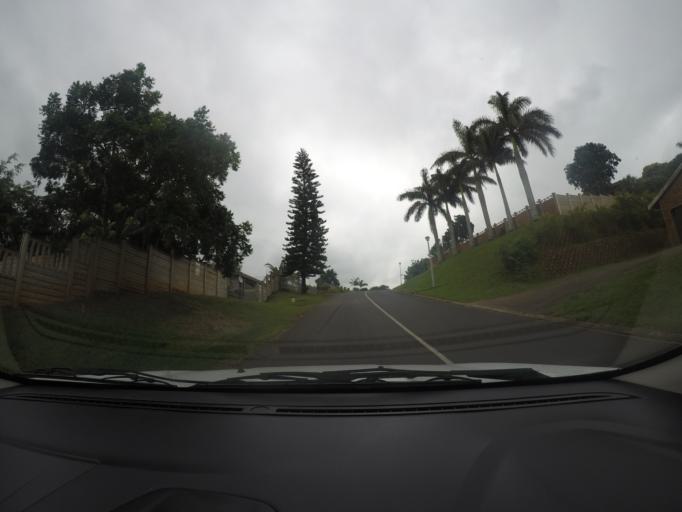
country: ZA
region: KwaZulu-Natal
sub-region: uThungulu District Municipality
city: Empangeni
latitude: -28.7628
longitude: 31.8873
